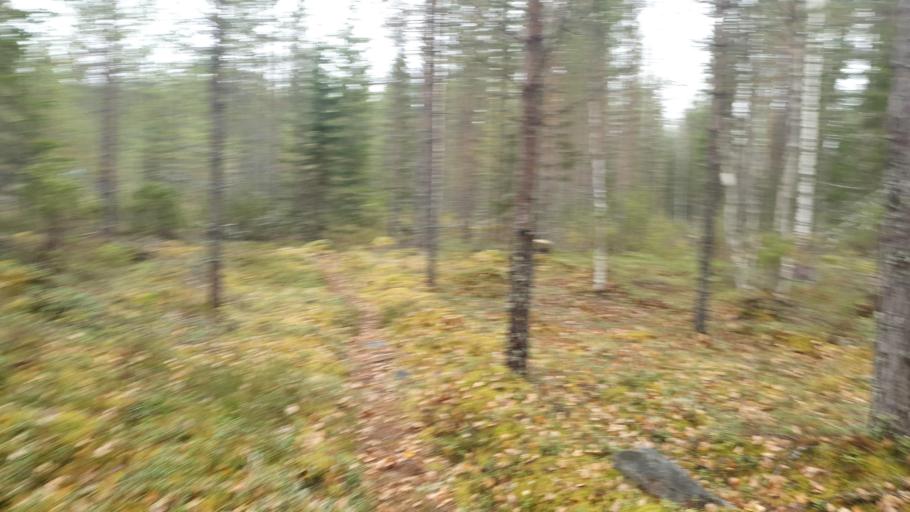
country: FI
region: Kainuu
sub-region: Kehys-Kainuu
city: Kuhmo
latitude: 64.1389
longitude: 29.3947
